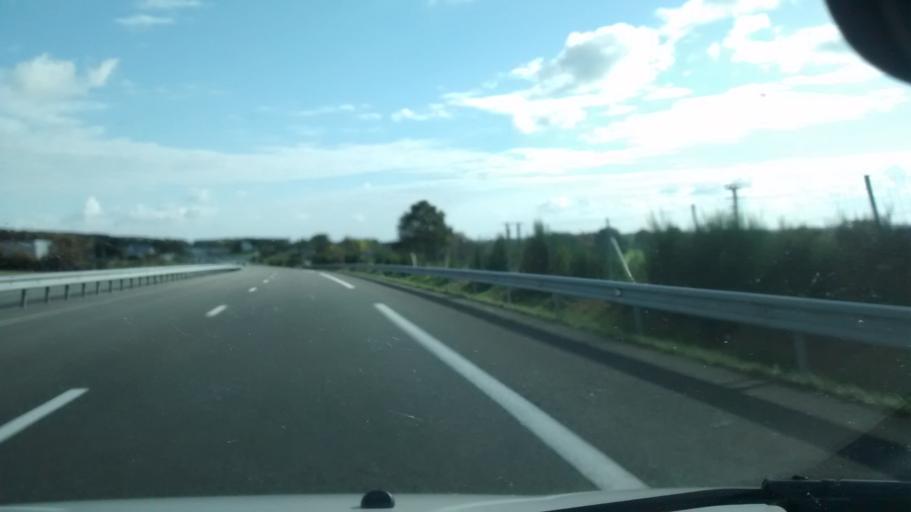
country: FR
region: Pays de la Loire
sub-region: Departement de Maine-et-Loire
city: Combree
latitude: 47.7202
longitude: -1.0363
